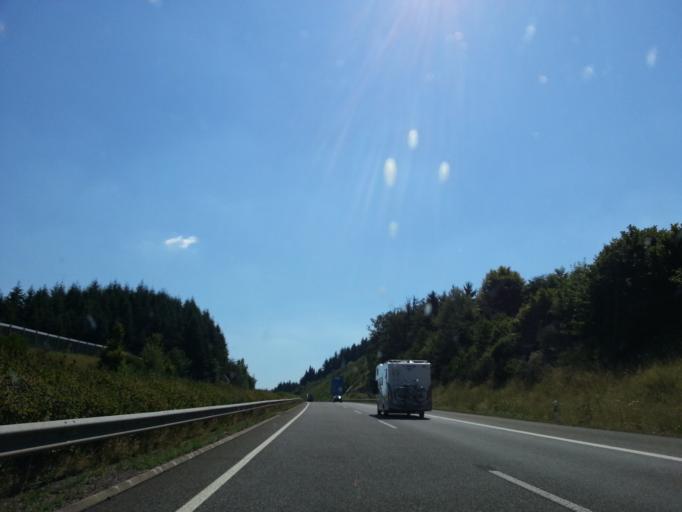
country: DE
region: Rheinland-Pfalz
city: Salmtal
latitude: 49.9545
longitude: 6.8565
